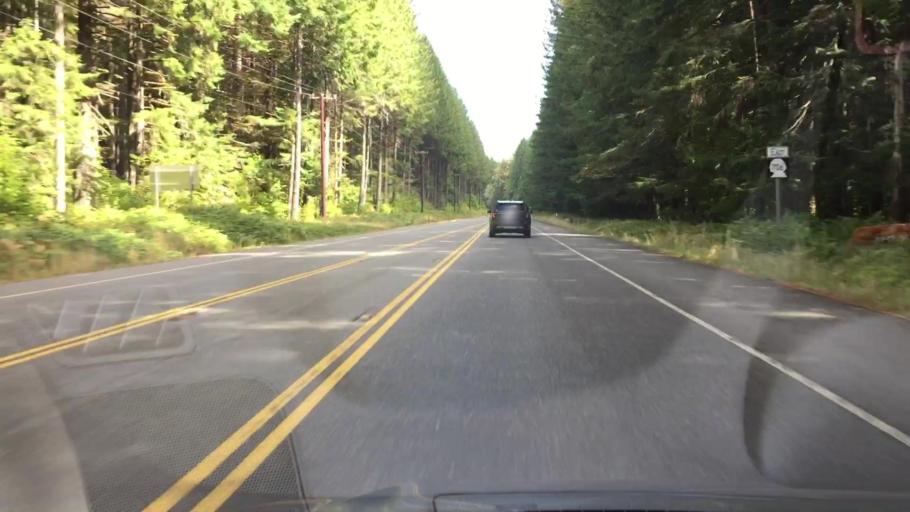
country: US
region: Washington
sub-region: Pierce County
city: Eatonville
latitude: 46.7543
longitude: -122.1182
